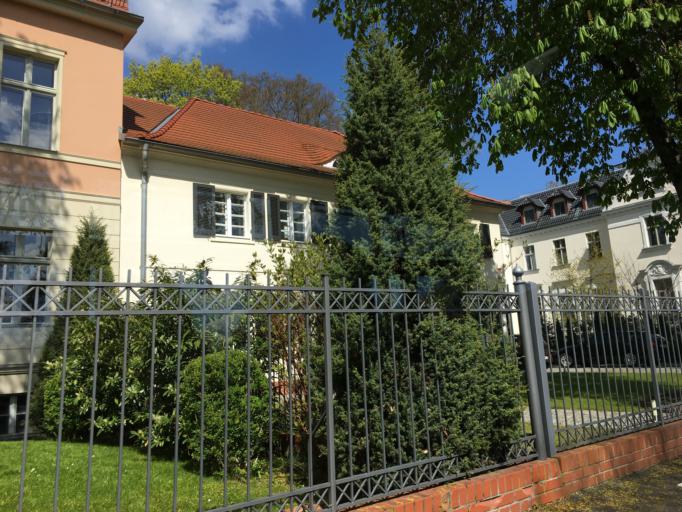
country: DE
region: Brandenburg
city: Potsdam
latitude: 52.4133
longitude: 13.0648
